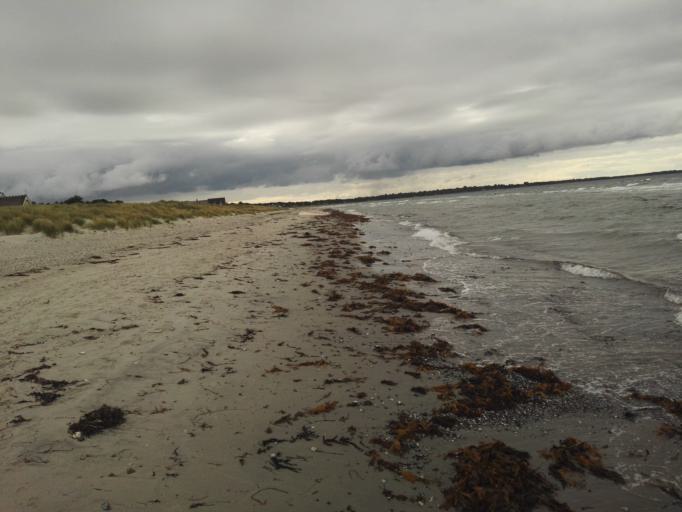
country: DK
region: Zealand
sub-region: Odsherred Kommune
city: Nykobing Sjaelland
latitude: 55.9442
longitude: 11.6712
